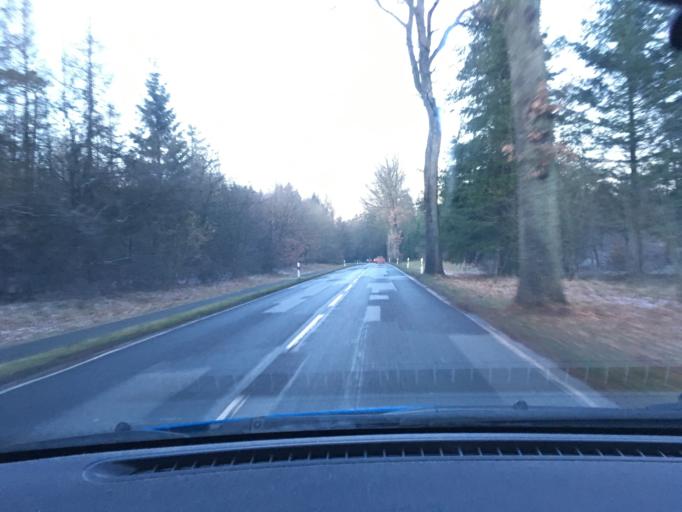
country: DE
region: Lower Saxony
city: Handeloh
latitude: 53.2709
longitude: 9.8786
